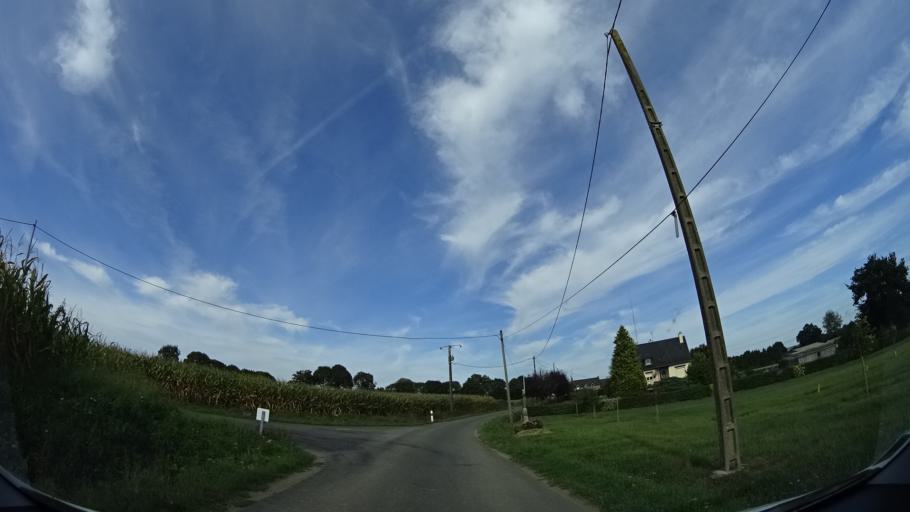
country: FR
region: Brittany
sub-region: Departement d'Ille-et-Vilaine
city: Romagne
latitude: 48.3201
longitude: -1.2766
